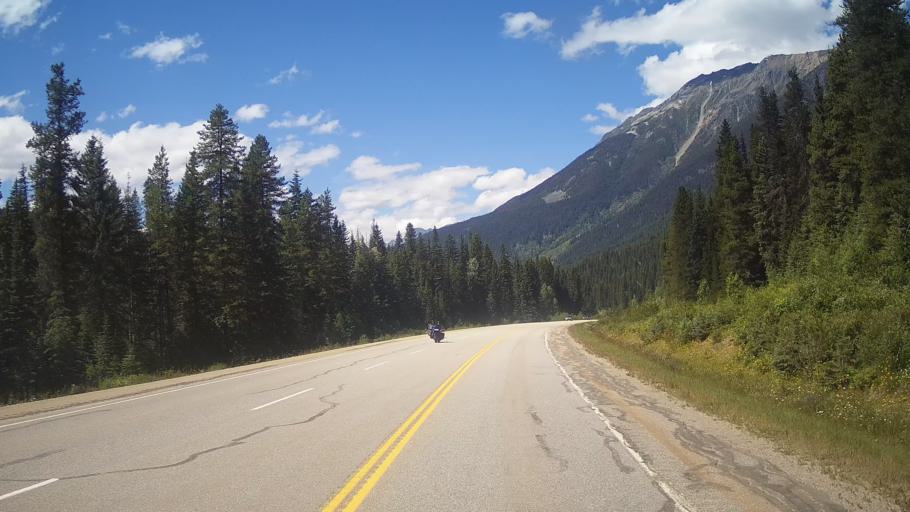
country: CA
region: Alberta
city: Grande Cache
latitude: 53.0094
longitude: -119.0633
